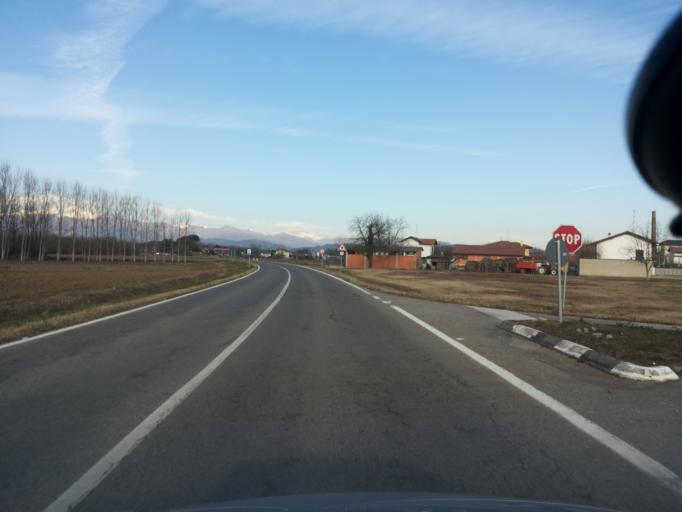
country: IT
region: Piedmont
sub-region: Provincia di Vercelli
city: Lenta
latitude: 45.5494
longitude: 8.3842
